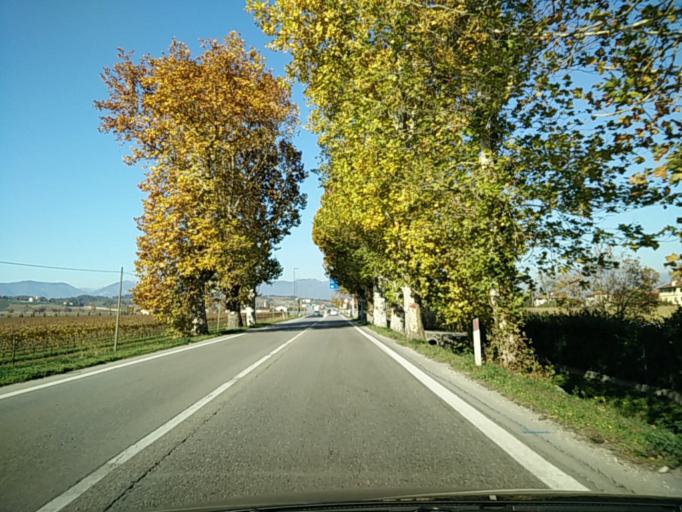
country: IT
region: Veneto
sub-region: Provincia di Treviso
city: Priula-Colfosco
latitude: 45.8345
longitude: 12.2558
